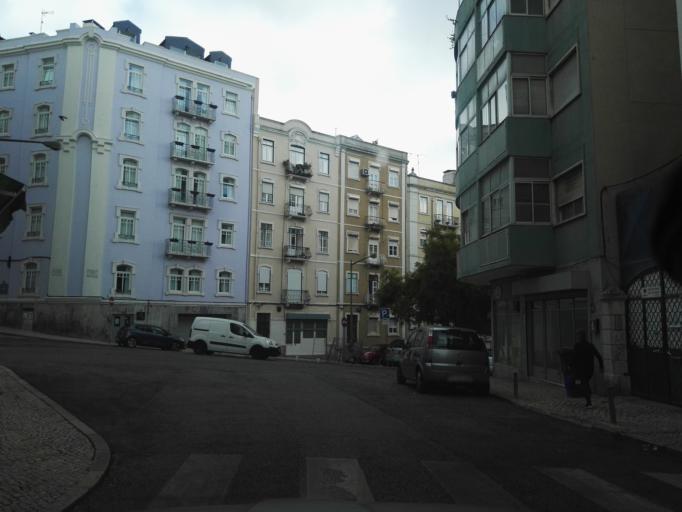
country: PT
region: Lisbon
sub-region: Lisbon
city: Lisbon
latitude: 38.7337
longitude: -9.1304
